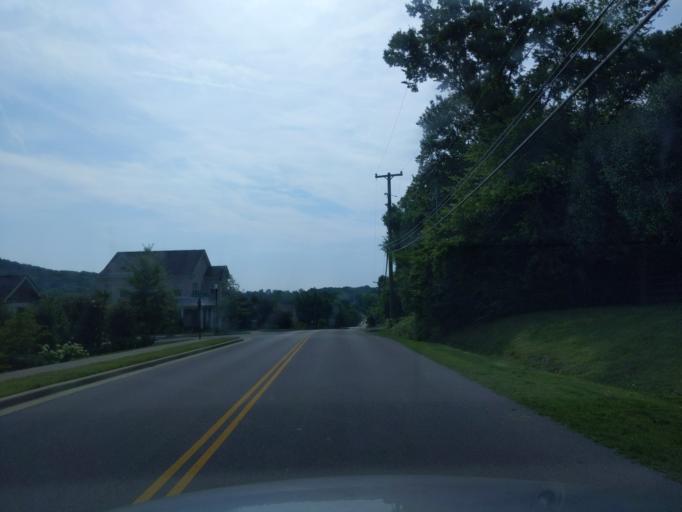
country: US
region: Tennessee
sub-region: Williamson County
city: Brentwood Estates
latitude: 36.0240
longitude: -86.7394
